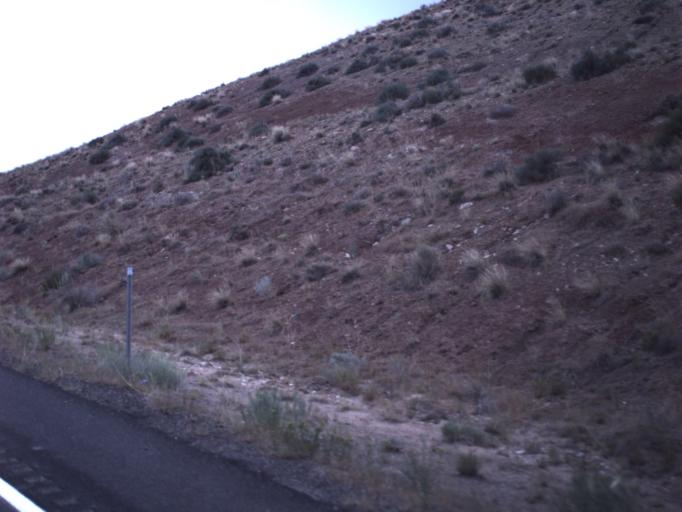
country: US
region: Utah
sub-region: Uintah County
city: Naples
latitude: 40.2705
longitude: -109.4594
